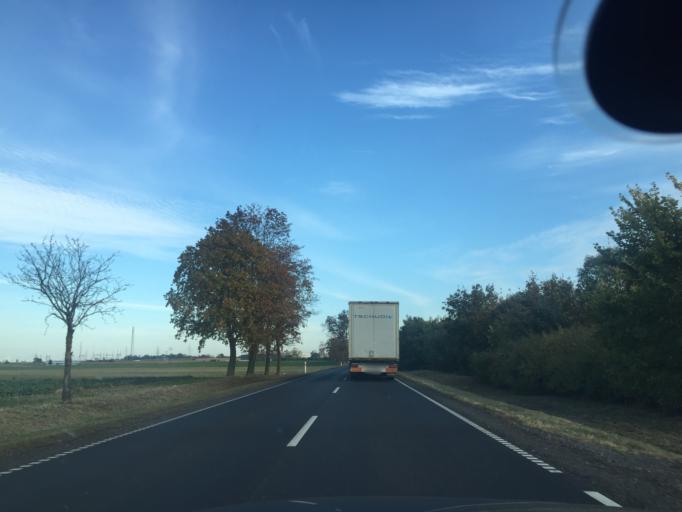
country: PL
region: Kujawsko-Pomorskie
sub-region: Powiat mogilenski
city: Strzelno
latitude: 52.6293
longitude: 18.1287
